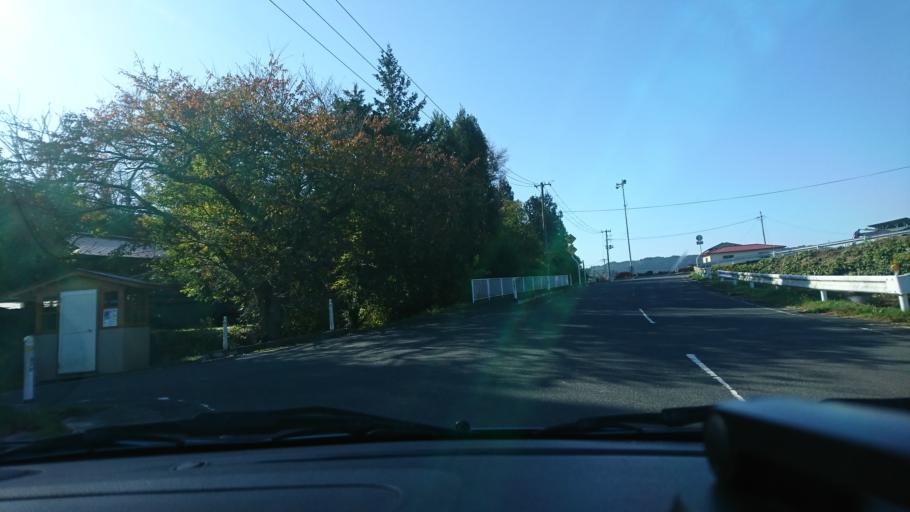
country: JP
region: Iwate
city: Ichinoseki
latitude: 38.8378
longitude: 141.2698
